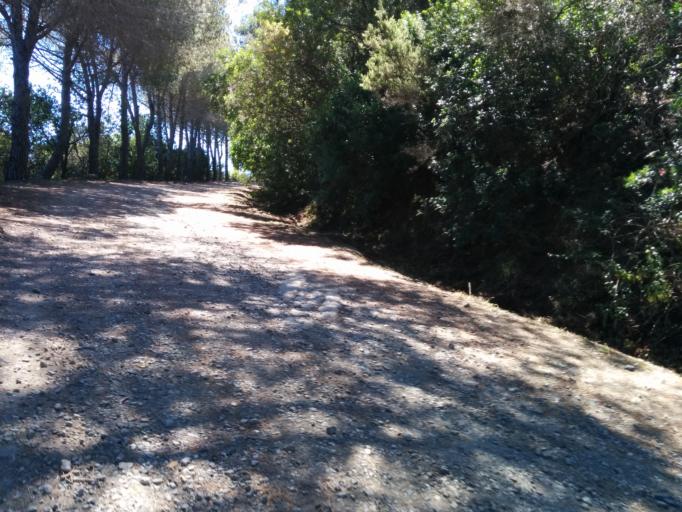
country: IT
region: Tuscany
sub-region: Provincia di Livorno
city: Portoferraio
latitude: 42.7574
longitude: 10.3176
